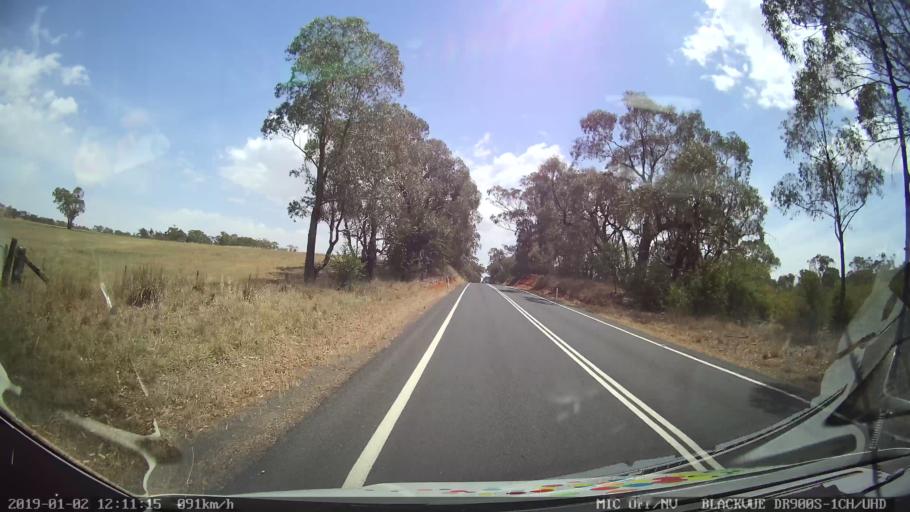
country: AU
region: New South Wales
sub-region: Young
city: Young
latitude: -34.4513
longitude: 148.2579
